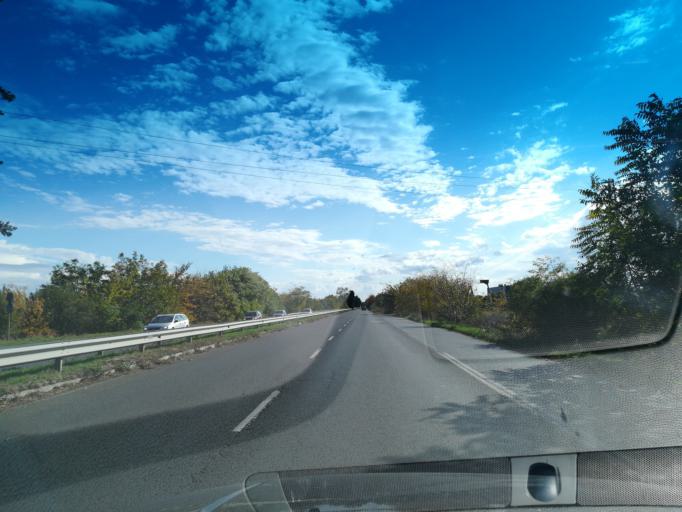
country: BG
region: Stara Zagora
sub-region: Obshtina Stara Zagora
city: Stara Zagora
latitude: 42.3923
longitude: 25.6464
